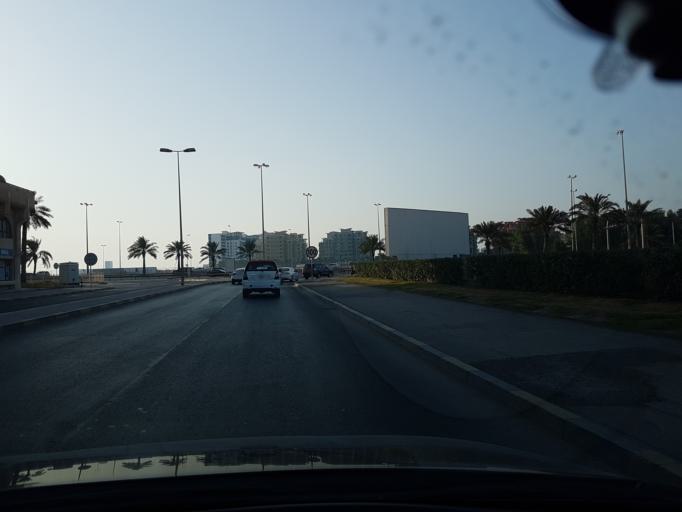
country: BH
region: Manama
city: Jidd Hafs
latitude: 26.2324
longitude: 50.5668
